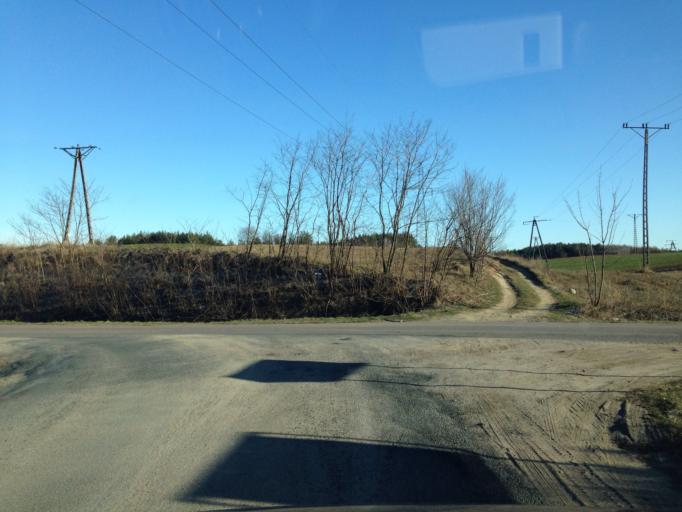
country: PL
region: Warmian-Masurian Voivodeship
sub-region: Powiat nowomiejski
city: Nowe Miasto Lubawskie
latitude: 53.4040
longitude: 19.6088
